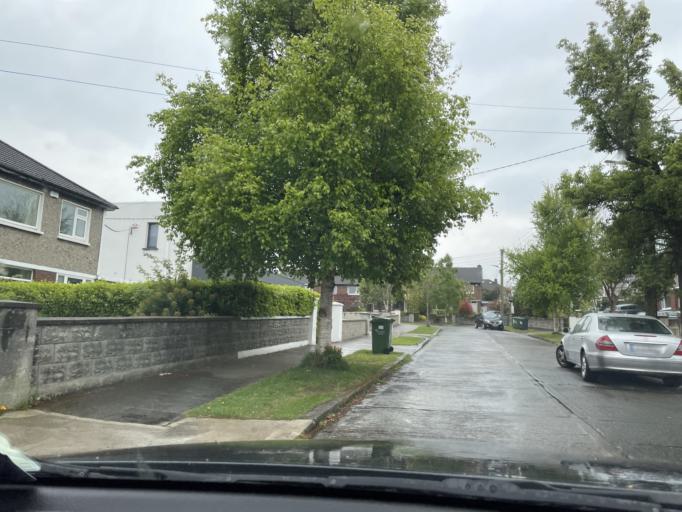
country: IE
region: Leinster
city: Dundrum
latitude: 53.2912
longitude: -6.2537
